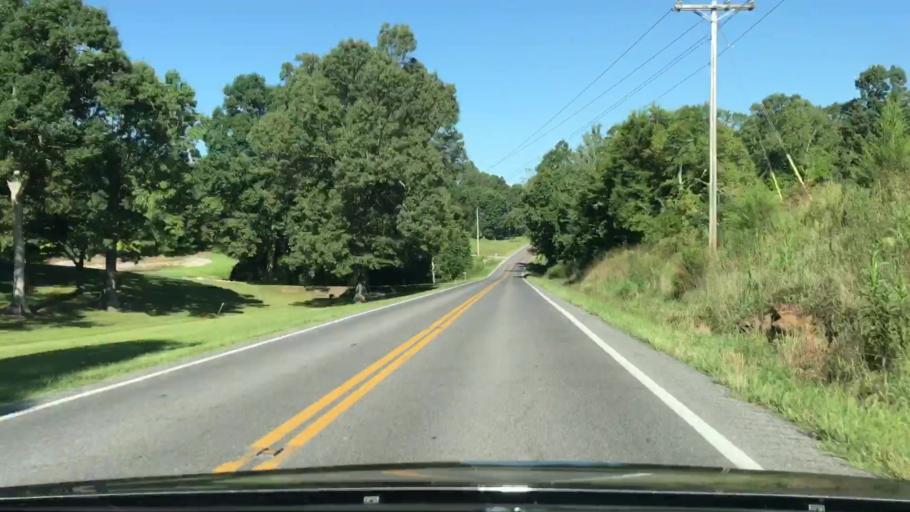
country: US
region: Kentucky
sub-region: Graves County
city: Mayfield
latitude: 36.7733
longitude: -88.5010
